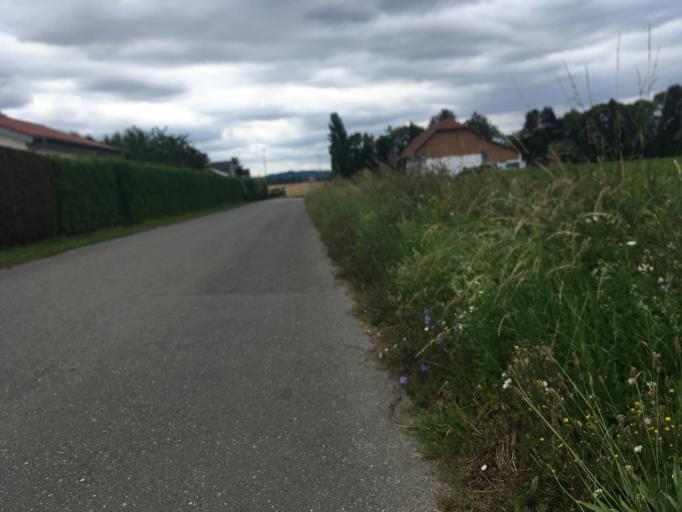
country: CH
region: Fribourg
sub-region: Broye District
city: Estavayer-le-Lac
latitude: 46.8655
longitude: 6.8842
